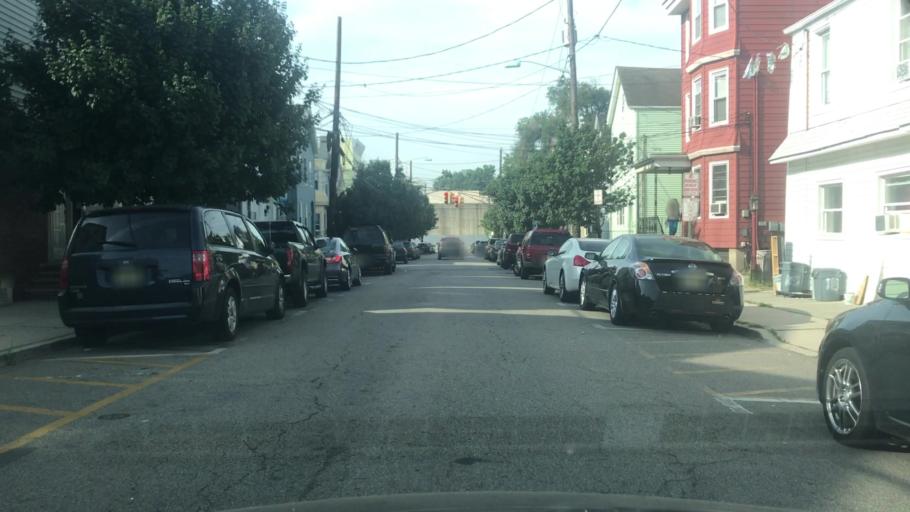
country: US
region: New Jersey
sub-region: Hudson County
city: East Newark
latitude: 40.7488
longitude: -74.1619
